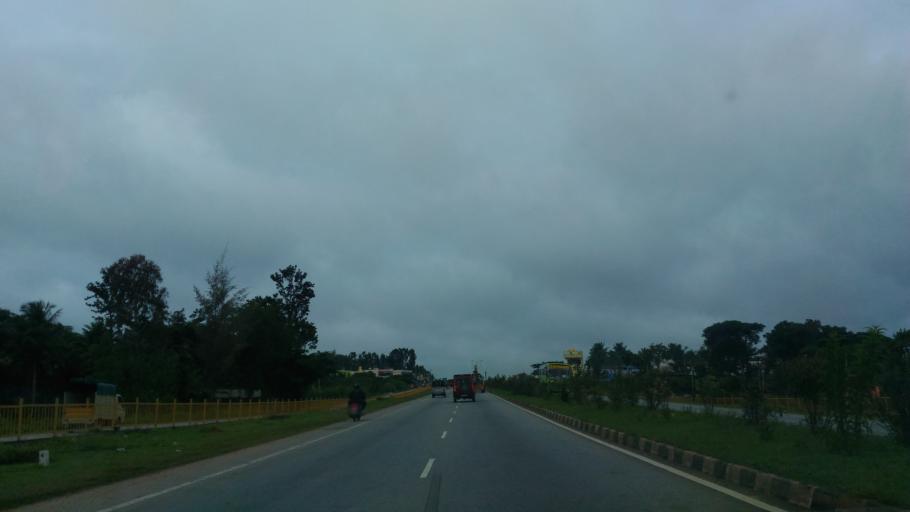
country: IN
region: Karnataka
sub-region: Ramanagara
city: Magadi
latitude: 13.0590
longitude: 77.1622
